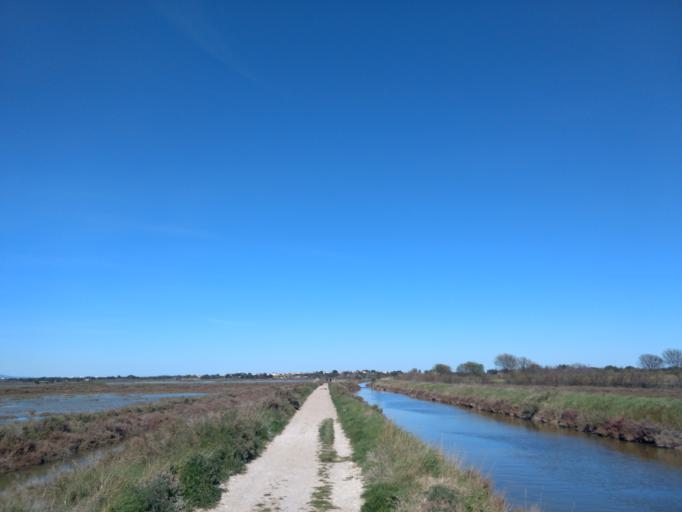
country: FR
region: Languedoc-Roussillon
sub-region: Departement de l'Herault
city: Villeneuve-les-Maguelone
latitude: 43.5104
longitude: 3.8396
